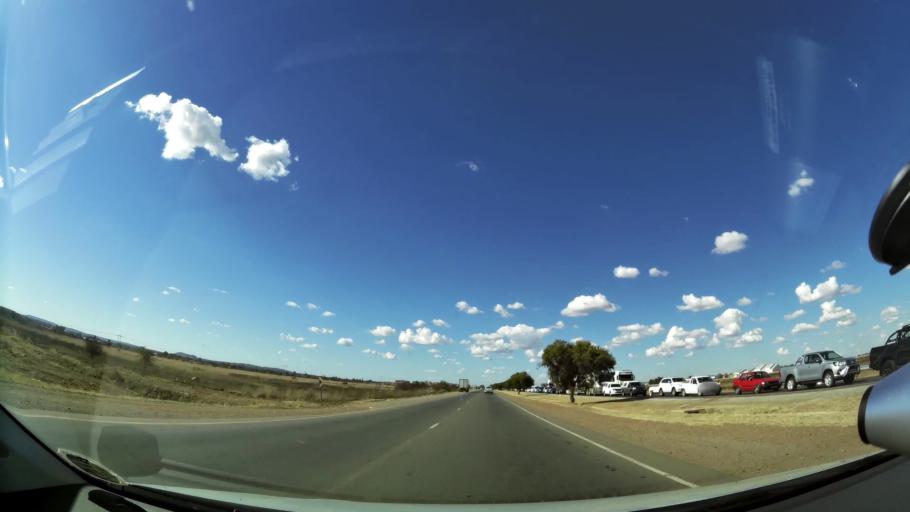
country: ZA
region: North-West
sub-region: Dr Kenneth Kaunda District Municipality
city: Klerksdorp
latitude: -26.8716
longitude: 26.6121
